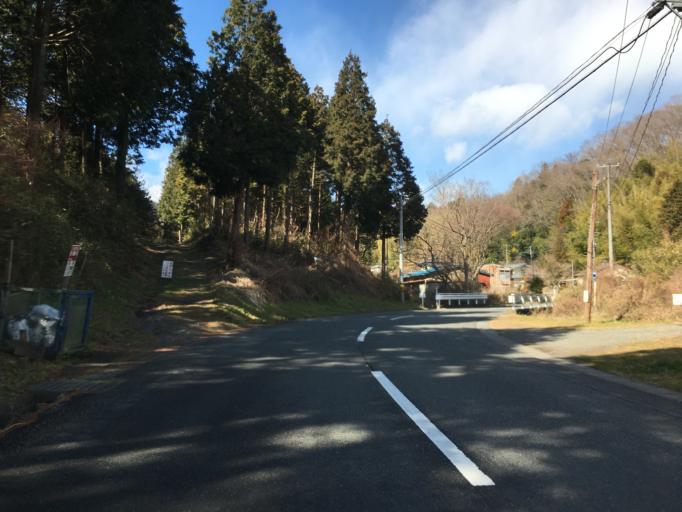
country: JP
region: Fukushima
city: Iwaki
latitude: 37.0134
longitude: 140.8229
